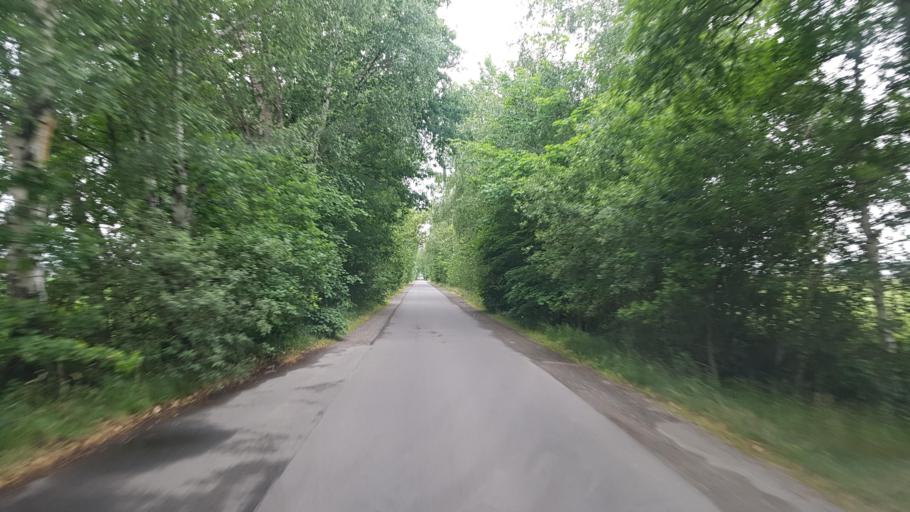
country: DE
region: Brandenburg
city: Schraden
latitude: 51.4322
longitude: 13.6939
